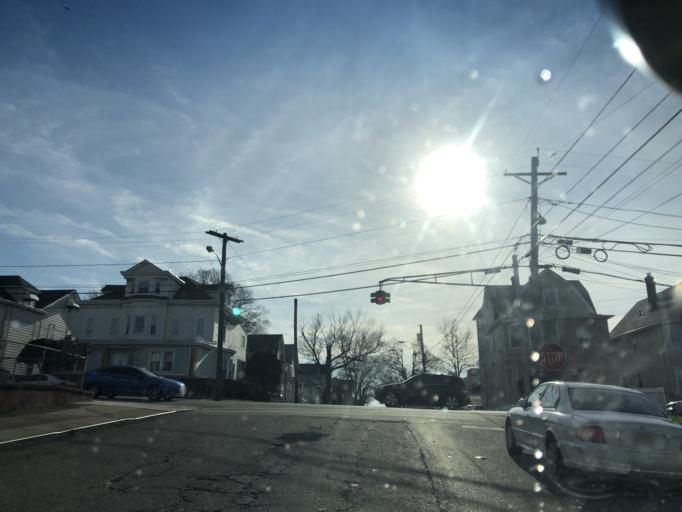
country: US
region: New Jersey
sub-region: Passaic County
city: Hawthorne
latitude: 40.9341
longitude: -74.1480
